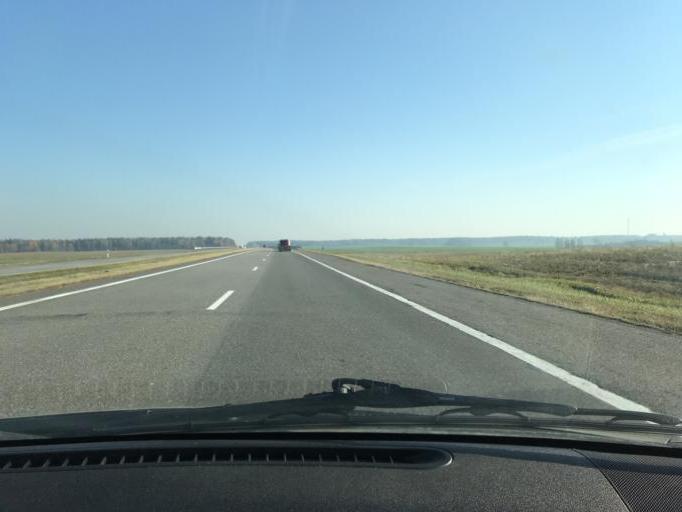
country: BY
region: Vitebsk
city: Talachyn
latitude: 54.4633
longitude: 29.7463
